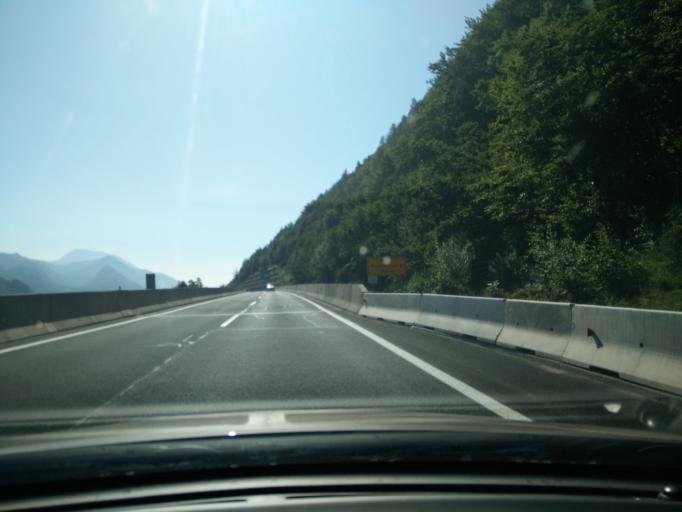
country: SI
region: Jesenice
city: Slovenski Javornik
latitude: 46.4234
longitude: 14.0776
